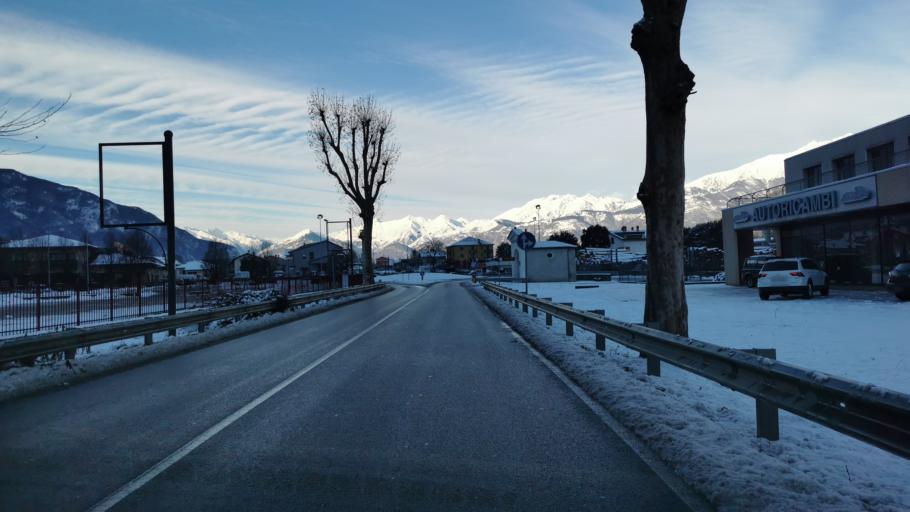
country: IT
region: Lombardy
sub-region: Provincia di Sondrio
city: Andalo Valtellino
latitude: 46.1369
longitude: 9.4789
